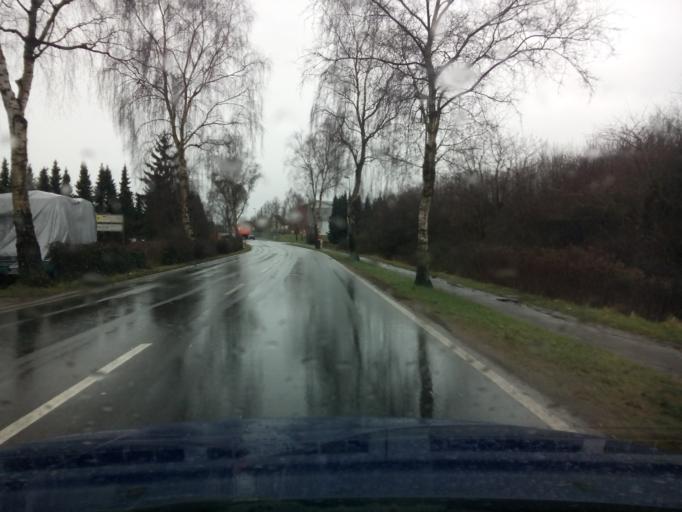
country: DE
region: Lower Saxony
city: Ritterhude
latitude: 53.1891
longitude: 8.7557
